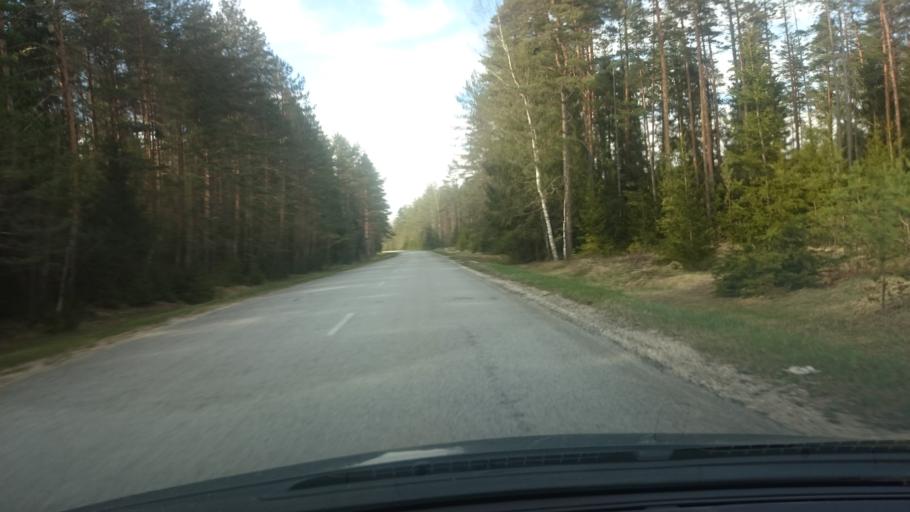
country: EE
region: Ida-Virumaa
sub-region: Toila vald
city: Voka
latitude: 59.1425
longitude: 27.6116
